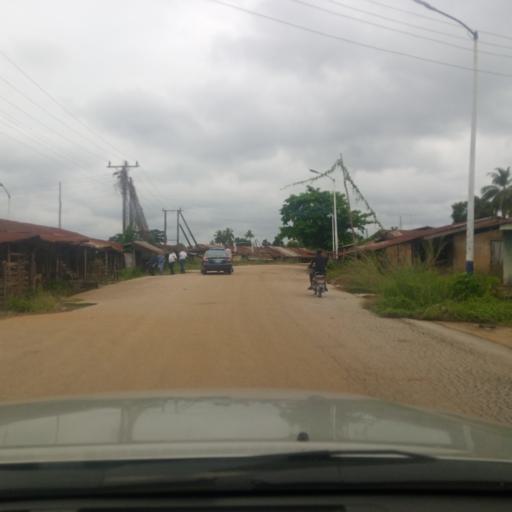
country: NG
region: Ebonyi
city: Effium
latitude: 6.6290
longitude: 8.0549
